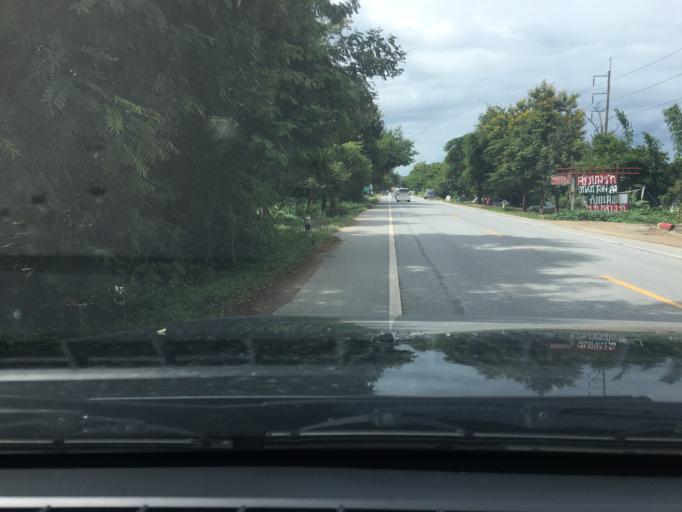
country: TH
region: Chiang Rai
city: Mae Suai
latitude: 19.5219
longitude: 99.4800
